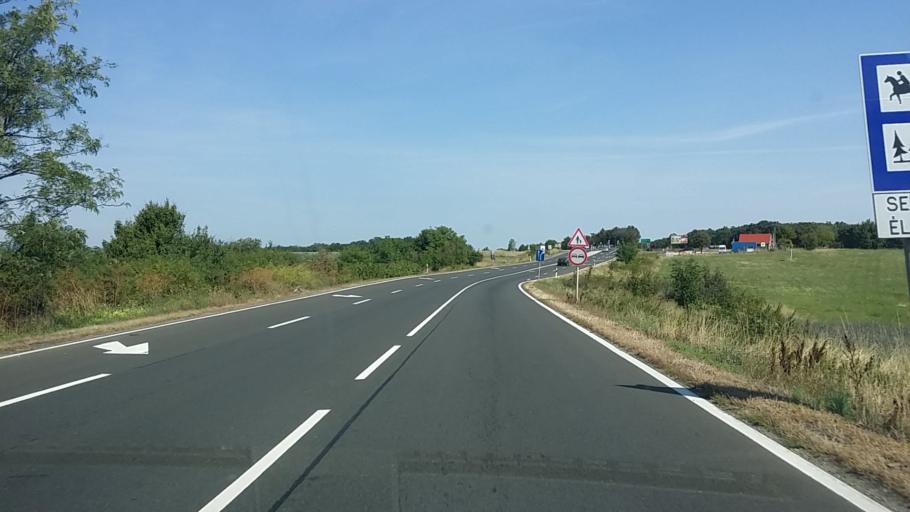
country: HU
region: Nograd
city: Retsag
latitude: 47.8797
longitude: 19.1045
